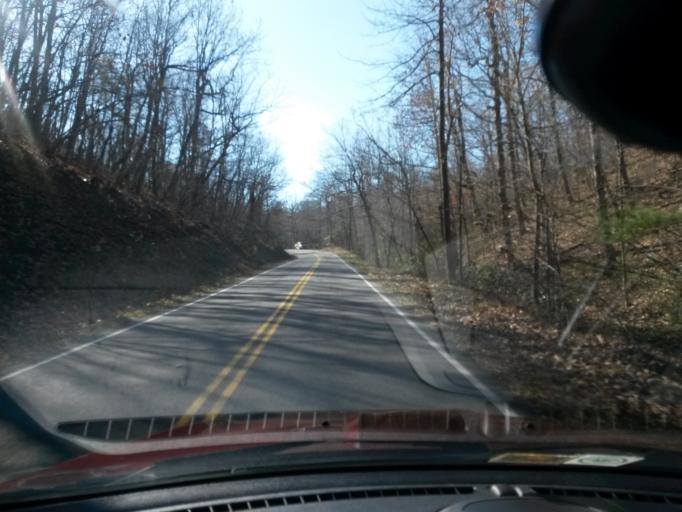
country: US
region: Virginia
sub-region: Botetourt County
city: Buchanan
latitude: 37.4868
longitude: -79.6679
